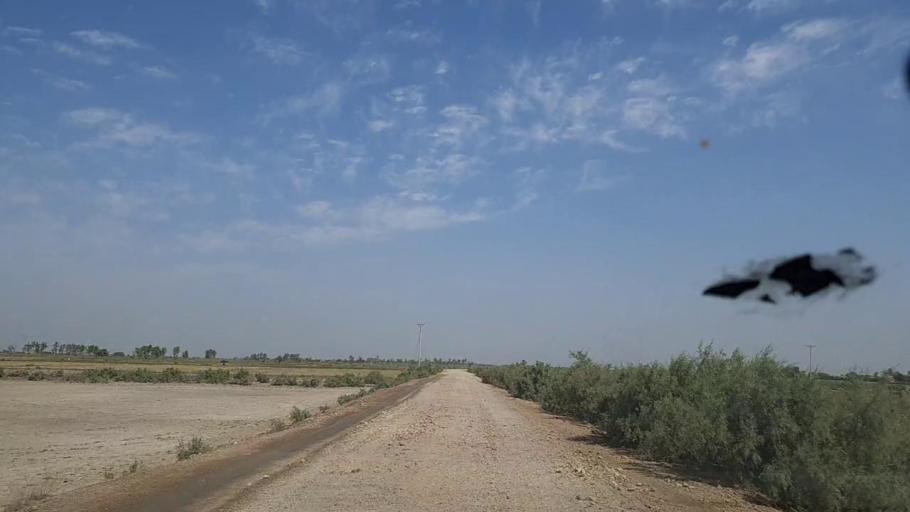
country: PK
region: Sindh
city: Daro Mehar
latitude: 24.6653
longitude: 68.0792
